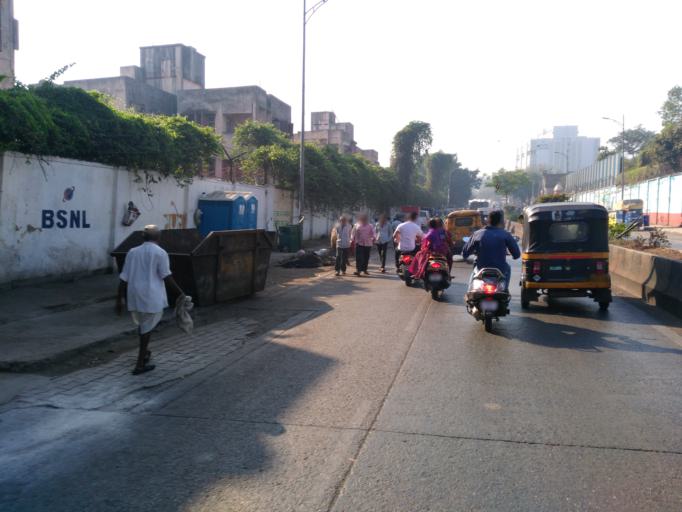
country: IN
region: Maharashtra
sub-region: Pune Division
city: Pune
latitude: 18.4956
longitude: 73.8693
